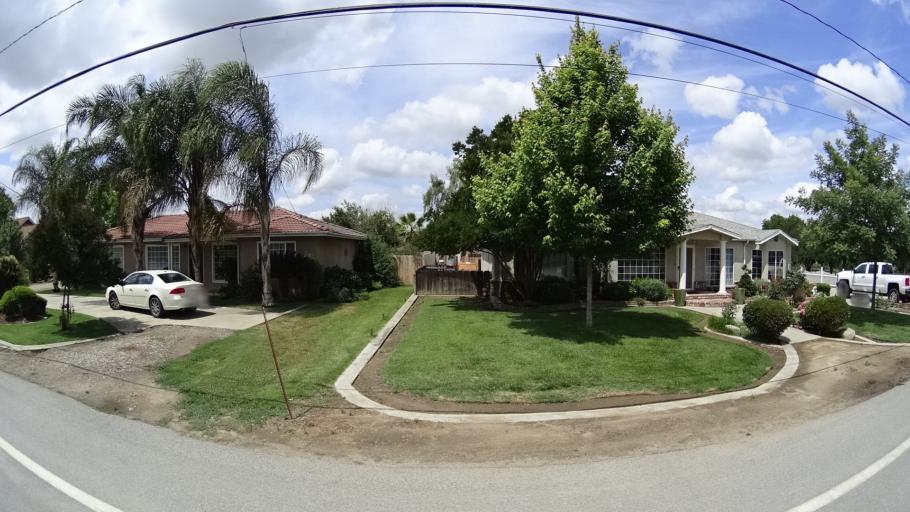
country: US
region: California
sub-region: Kings County
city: Lucerne
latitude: 36.3699
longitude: -119.6551
